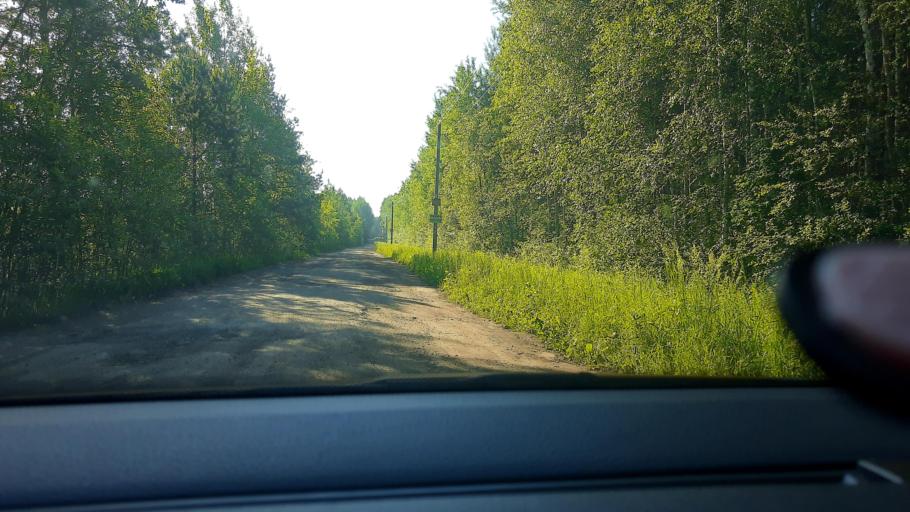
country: RU
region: Moskovskaya
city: Elektrogorsk
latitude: 55.8991
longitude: 38.7063
